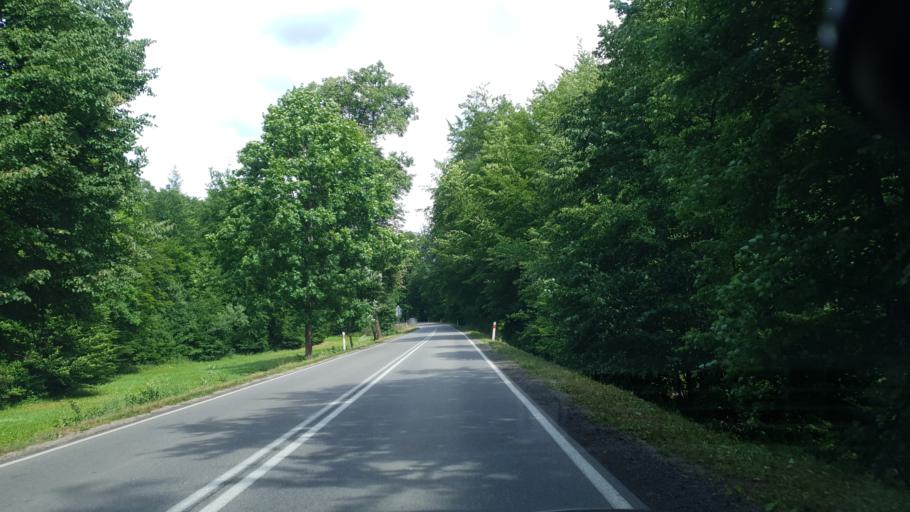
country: PL
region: Pomeranian Voivodeship
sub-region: Powiat kartuski
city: Kartuzy
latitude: 54.3170
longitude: 18.1680
